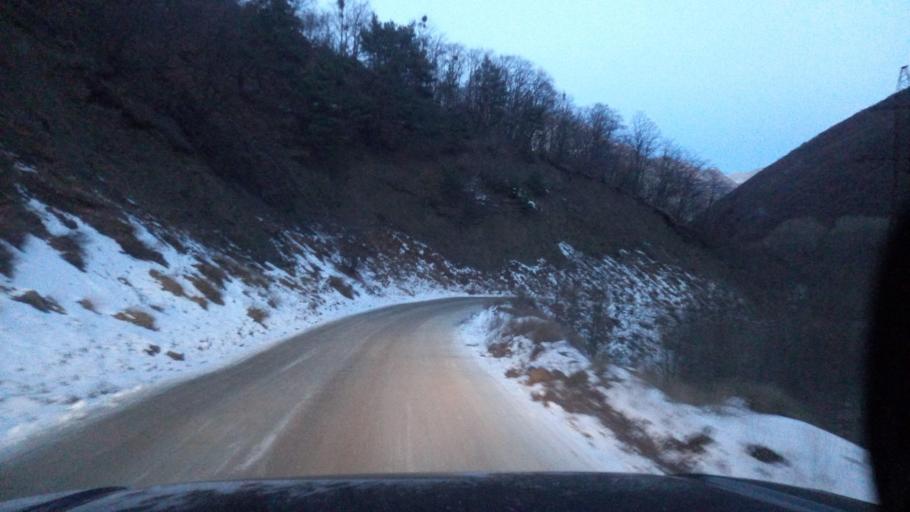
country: RU
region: Ingushetiya
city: Dzhayrakh
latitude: 42.8285
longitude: 44.6114
